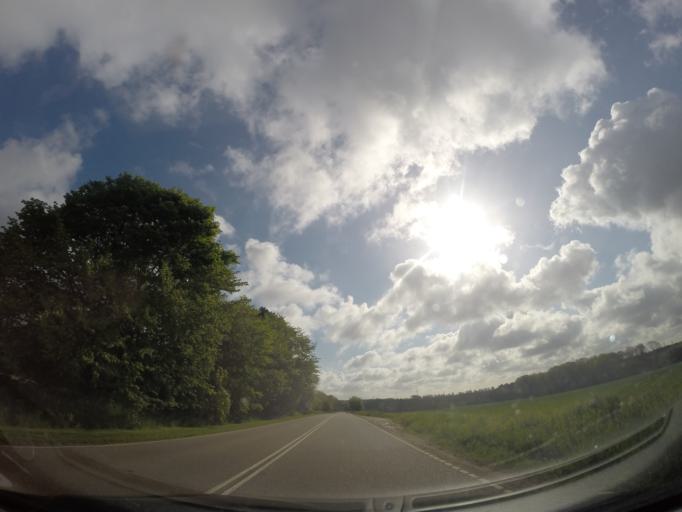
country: DK
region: Capital Region
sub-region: Hoje-Taastrup Kommune
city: Taastrup
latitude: 55.6821
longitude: 12.3063
